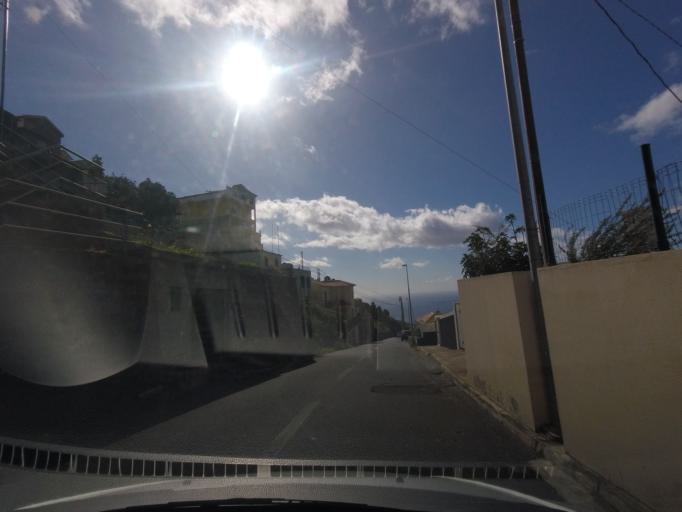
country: PT
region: Madeira
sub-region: Ribeira Brava
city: Campanario
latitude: 32.6616
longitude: -17.0202
